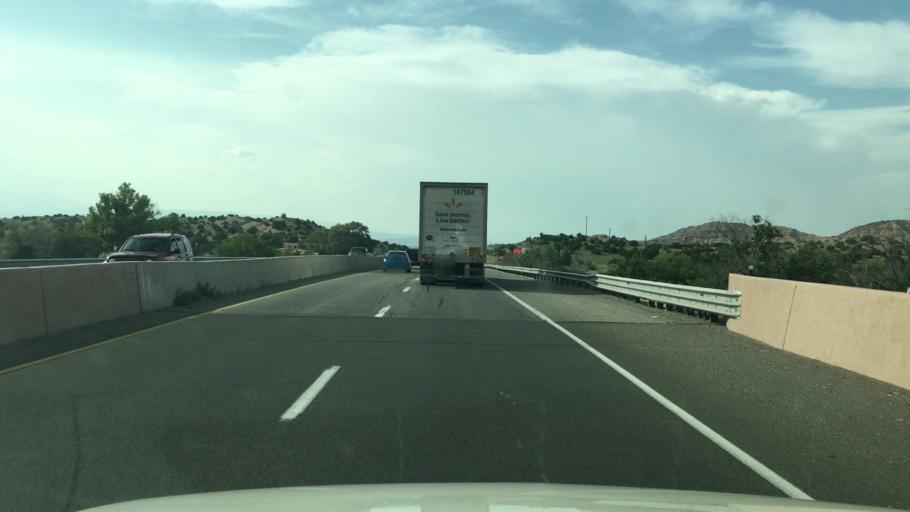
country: US
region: New Mexico
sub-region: Santa Fe County
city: Nambe
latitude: 35.8081
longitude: -105.9653
